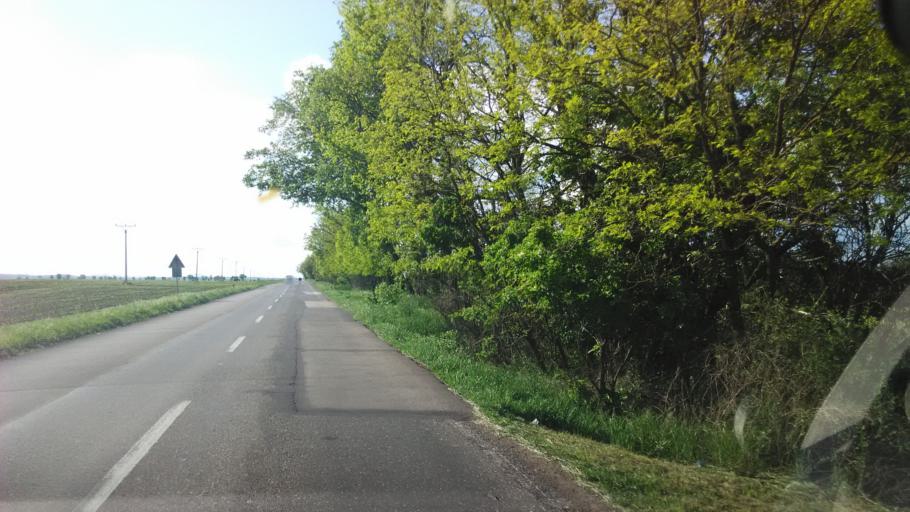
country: SK
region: Nitriansky
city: Levice
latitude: 48.1635
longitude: 18.5516
